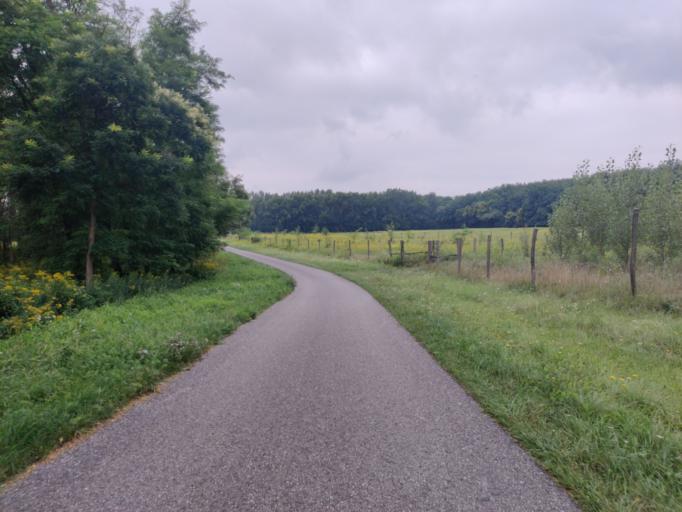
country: AT
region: Lower Austria
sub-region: Politischer Bezirk Tulln
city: Fels am Wagram
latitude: 48.3741
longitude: 15.8490
